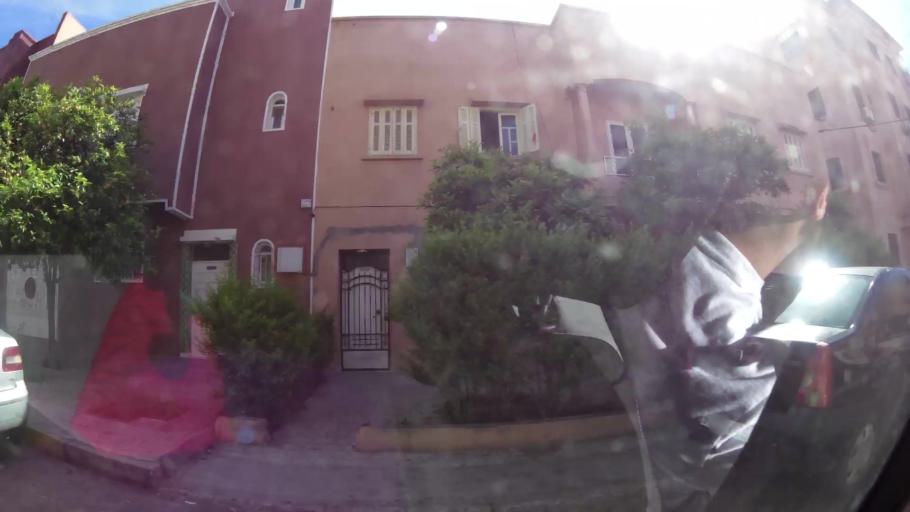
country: MA
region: Marrakech-Tensift-Al Haouz
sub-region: Marrakech
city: Marrakesh
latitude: 31.6570
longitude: -8.0167
